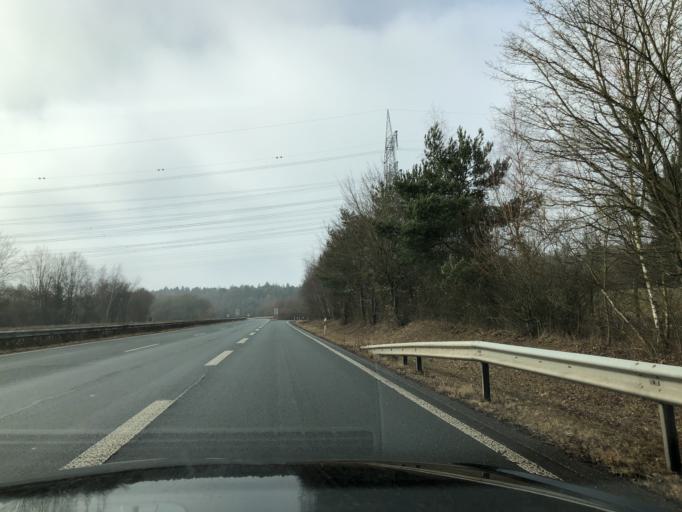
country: DE
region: Rheinland-Pfalz
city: Konigsfeld
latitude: 50.5307
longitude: 7.1898
